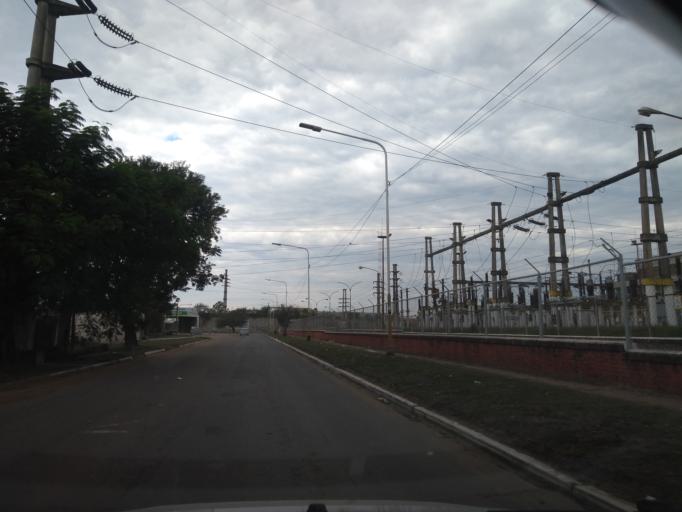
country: AR
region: Chaco
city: Barranqueras
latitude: -27.4899
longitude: -58.9285
